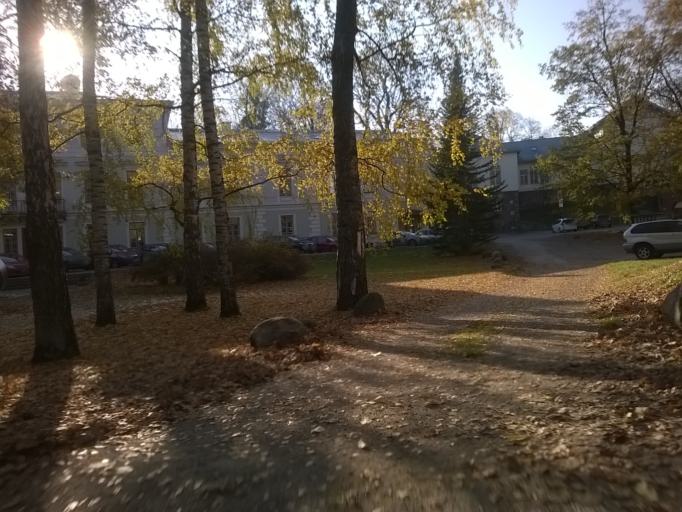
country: EE
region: Tartu
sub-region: Tartu linn
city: Tartu
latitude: 58.3800
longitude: 26.7162
